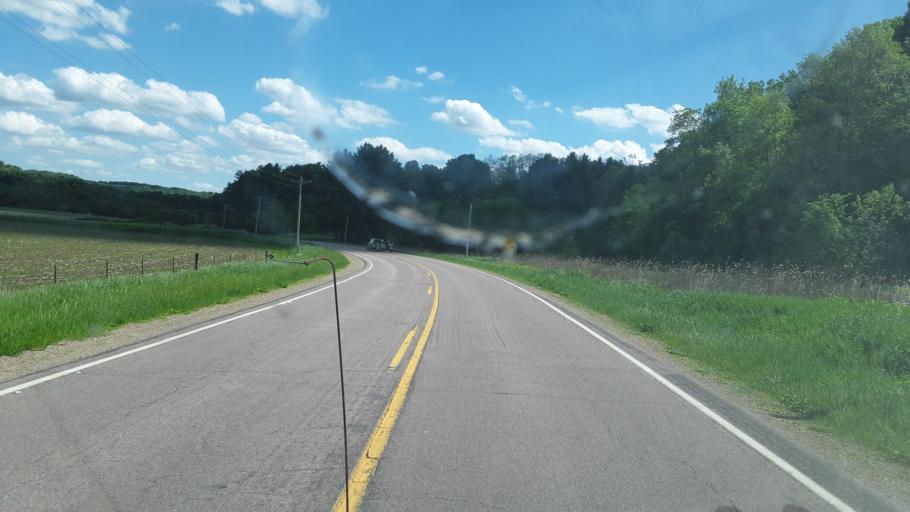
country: US
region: Wisconsin
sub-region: Richland County
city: Richland Center
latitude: 43.4186
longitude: -90.2434
